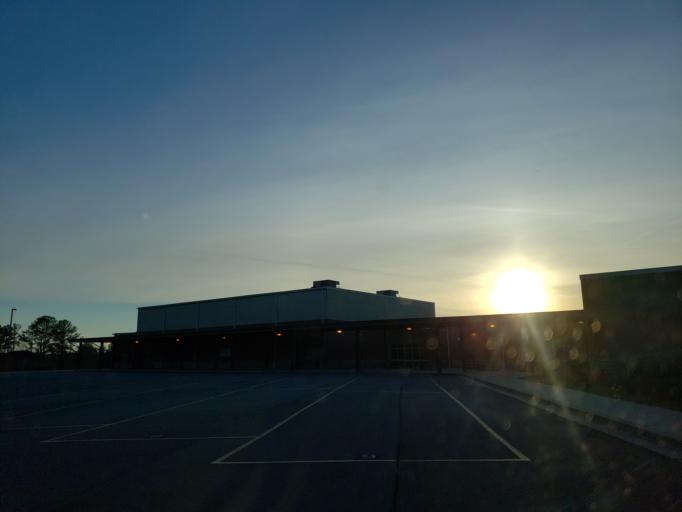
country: US
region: Georgia
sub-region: Cobb County
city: Acworth
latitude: 34.0284
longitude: -84.7348
